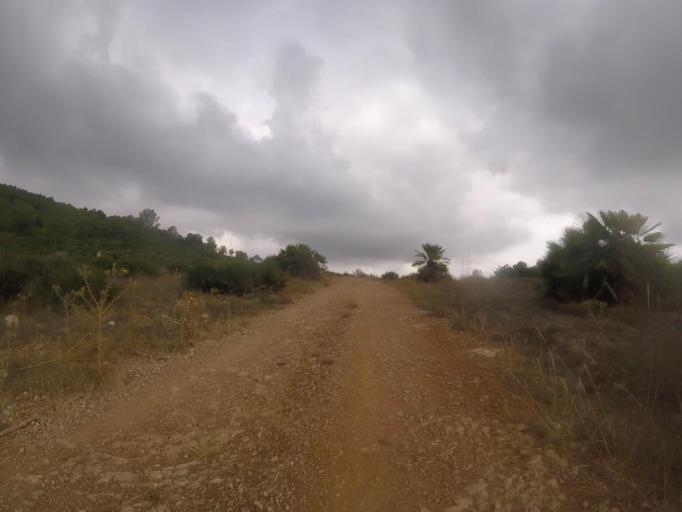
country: ES
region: Valencia
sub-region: Provincia de Castello
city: Santa Magdalena de Pulpis
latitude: 40.3248
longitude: 0.2899
